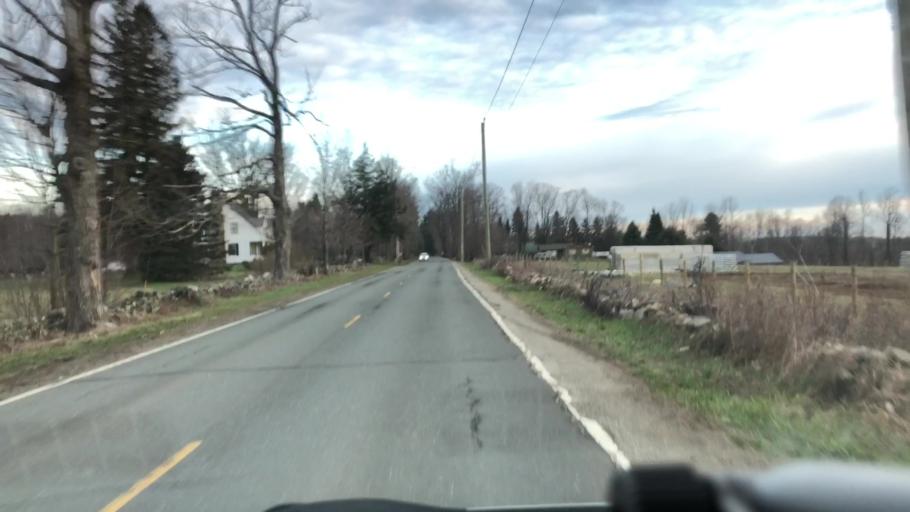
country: US
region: Massachusetts
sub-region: Hampshire County
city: Chesterfield
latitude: 42.4170
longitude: -72.9396
